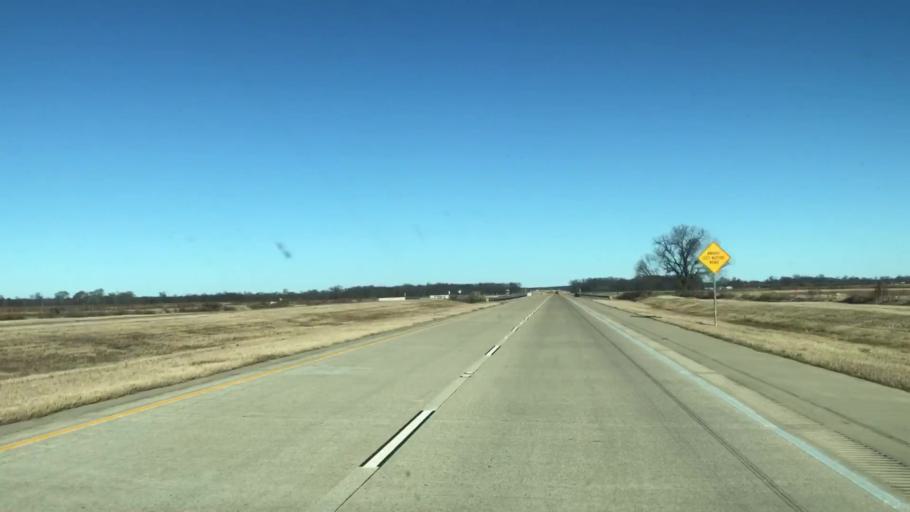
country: US
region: Louisiana
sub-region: Caddo Parish
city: Oil City
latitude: 32.7292
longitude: -93.8727
